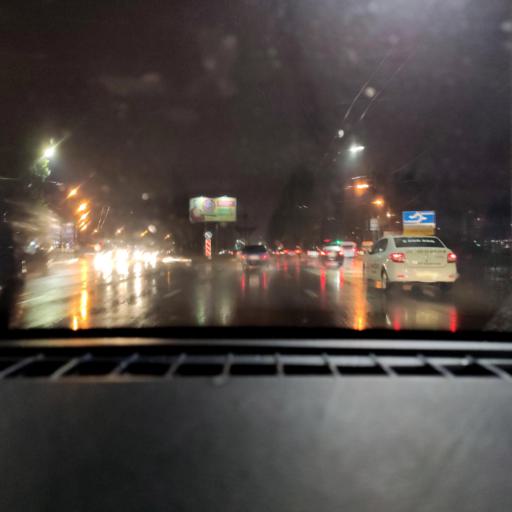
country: RU
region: Voronezj
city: Voronezh
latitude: 51.6879
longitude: 39.2654
